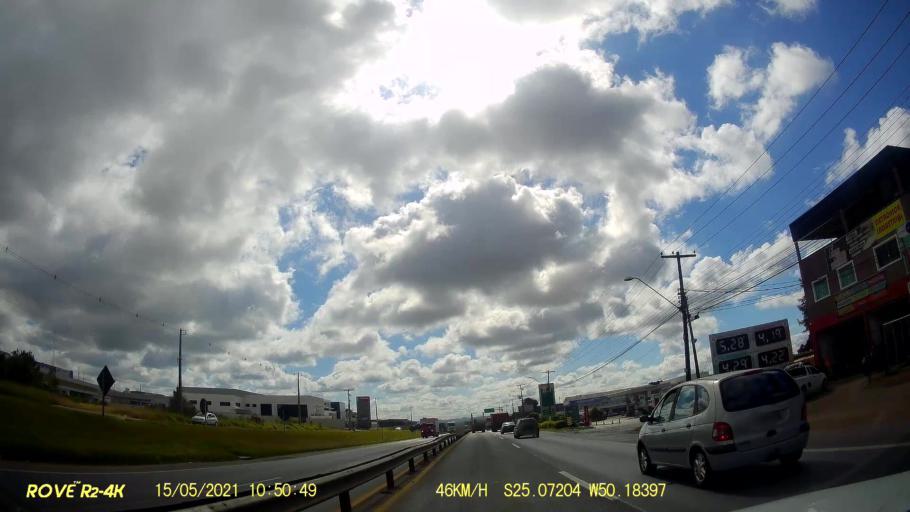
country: BR
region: Parana
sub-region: Ponta Grossa
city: Ponta Grossa
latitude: -25.0720
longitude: -50.1840
